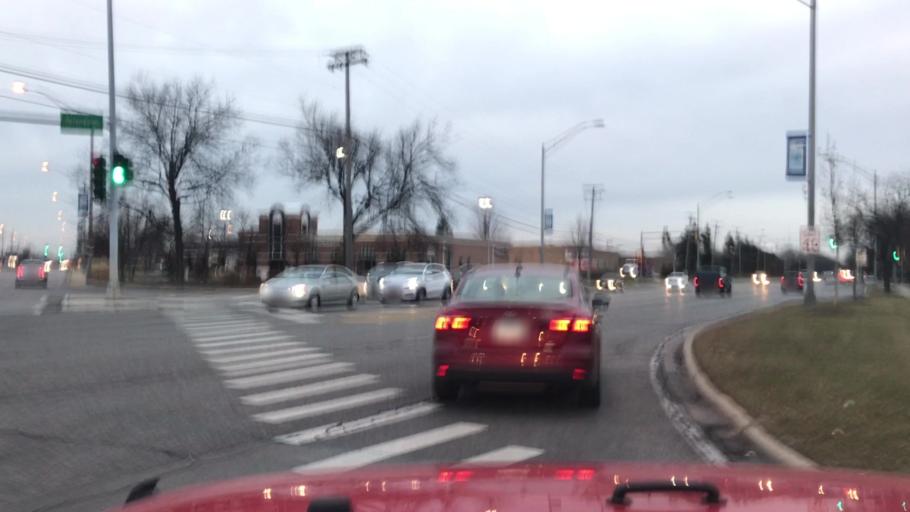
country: US
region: Illinois
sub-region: Cook County
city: Arlington Heights
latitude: 42.1127
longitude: -87.9802
